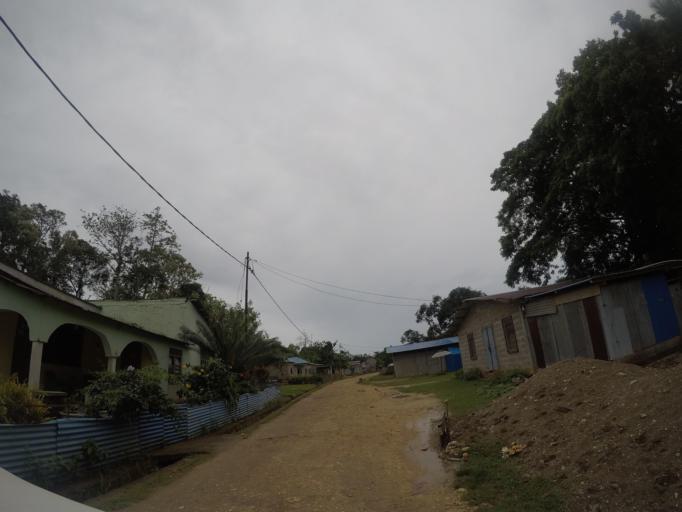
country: TL
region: Lautem
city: Lospalos
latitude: -8.5219
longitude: 127.0044
